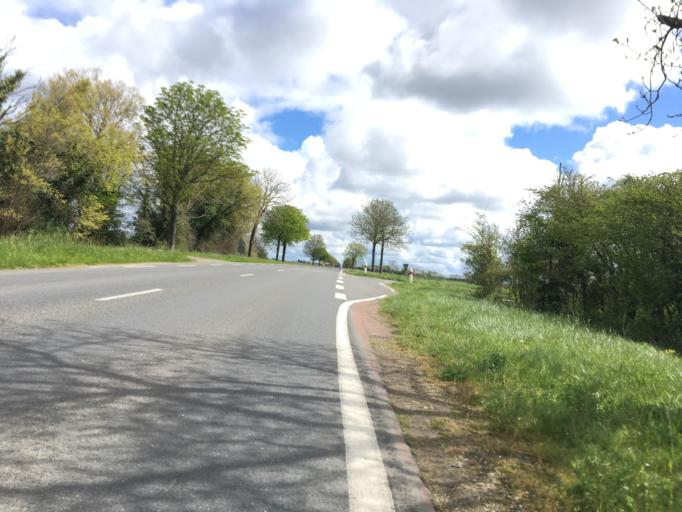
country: FR
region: Poitou-Charentes
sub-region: Departement de la Charente-Maritime
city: Le Thou
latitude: 46.1013
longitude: -0.8700
